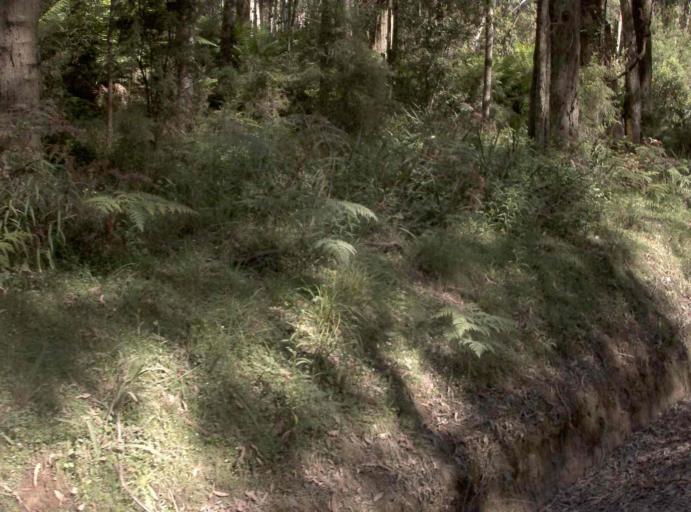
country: AU
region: New South Wales
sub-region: Bombala
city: Bombala
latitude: -37.2426
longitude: 148.7575
